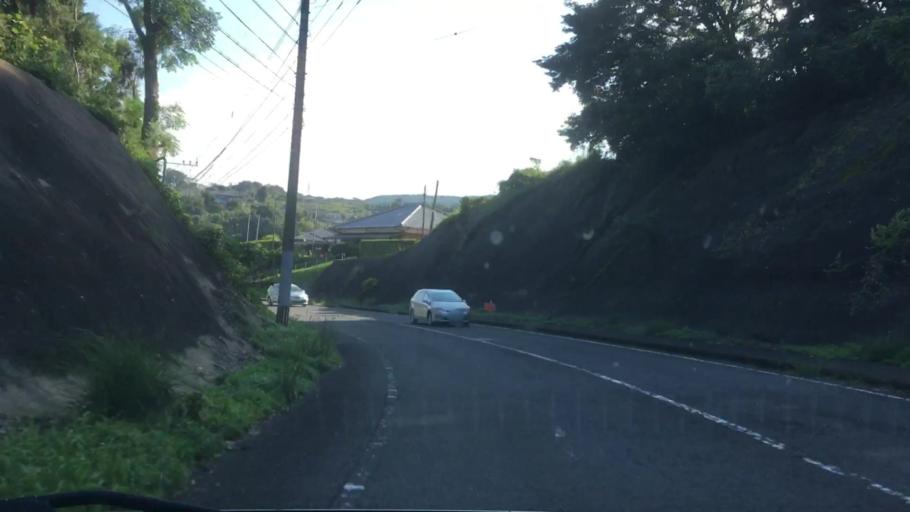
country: JP
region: Nagasaki
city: Sasebo
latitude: 32.9900
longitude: 129.6506
